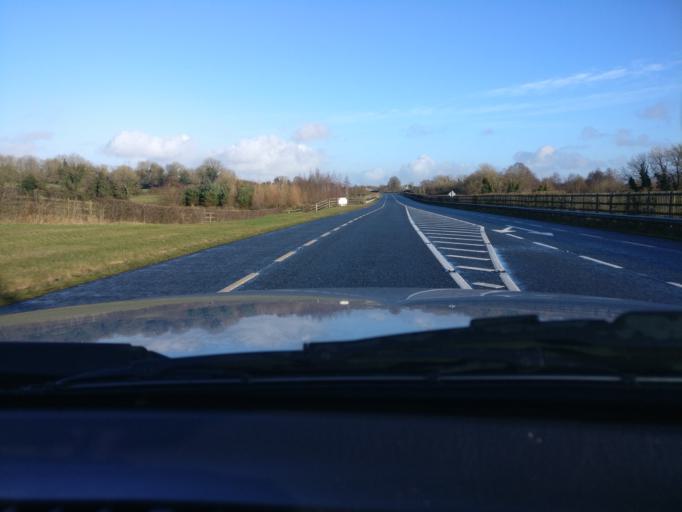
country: IE
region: Leinster
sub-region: An Iarmhi
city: An Muileann gCearr
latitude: 53.5488
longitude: -7.2850
